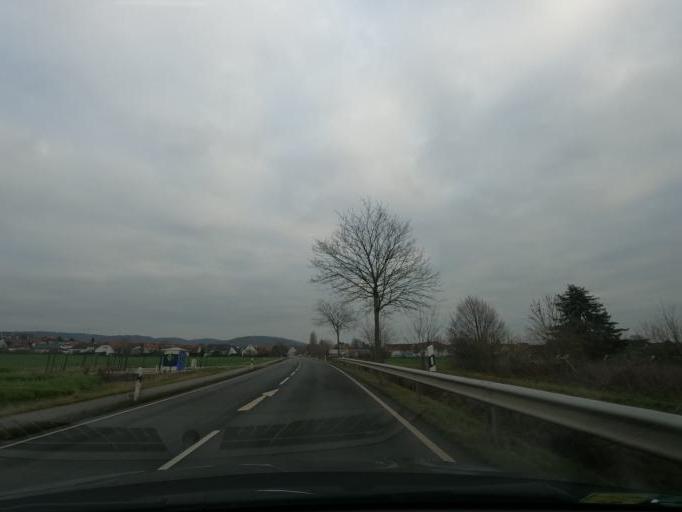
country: DE
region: Lower Saxony
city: Kissenbruck
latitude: 52.1472
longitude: 10.6020
